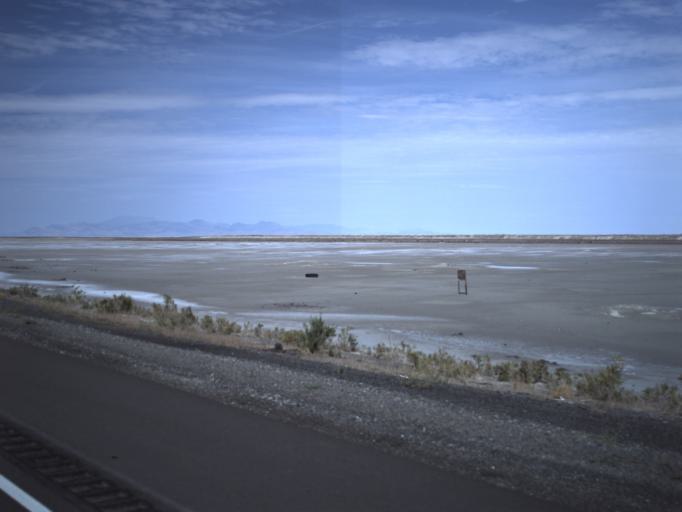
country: US
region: Utah
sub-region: Tooele County
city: Wendover
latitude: 40.7280
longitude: -113.2938
